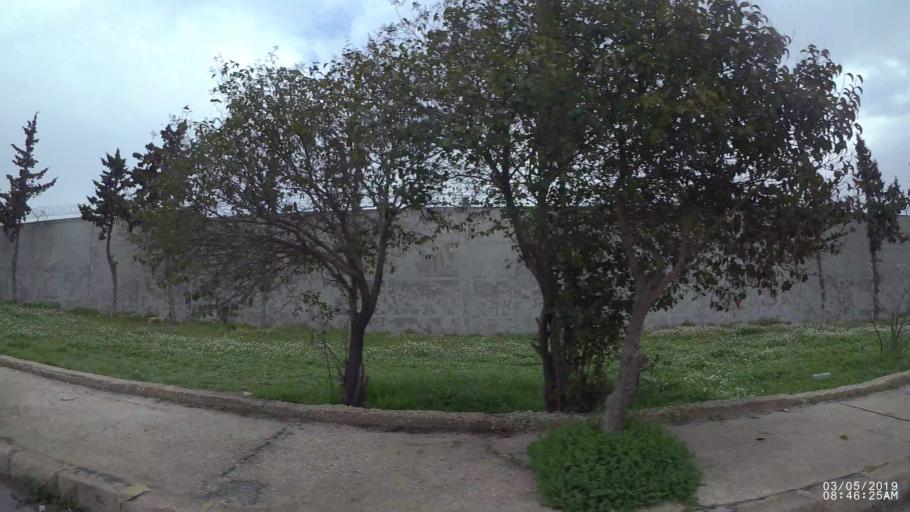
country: JO
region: Amman
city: Amman
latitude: 31.9611
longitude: 35.9403
